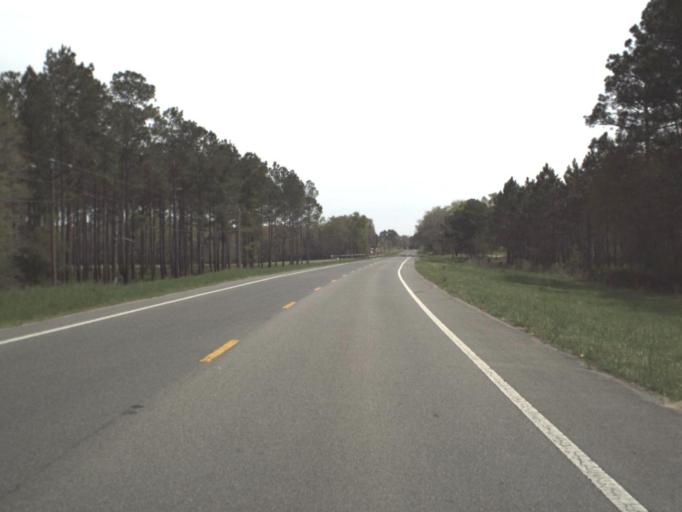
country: US
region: Alabama
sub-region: Geneva County
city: Geneva
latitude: 30.9480
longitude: -85.8319
